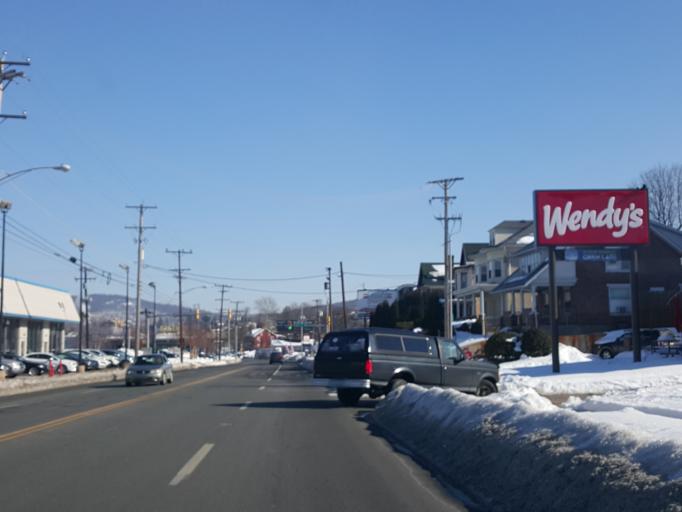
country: US
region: Pennsylvania
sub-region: Berks County
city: Kenhorst
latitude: 40.3148
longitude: -75.9425
